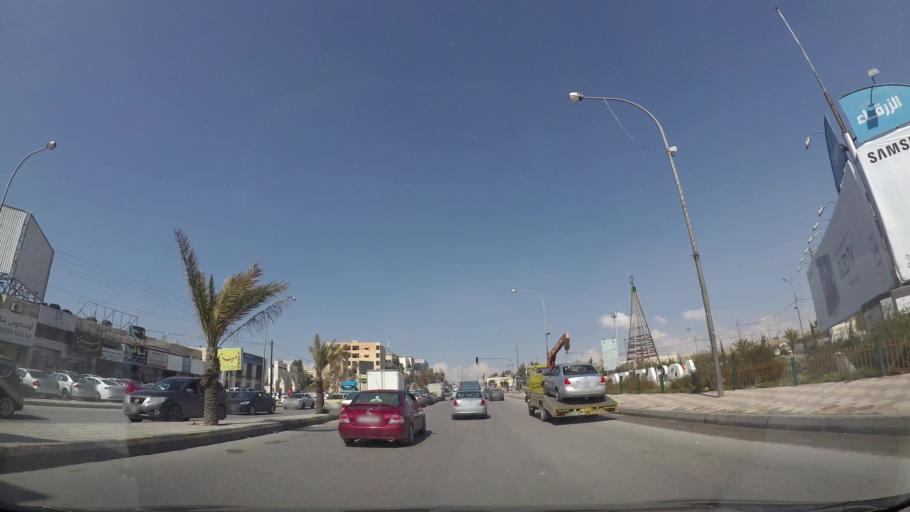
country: JO
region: Zarqa
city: Zarqa
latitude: 32.0506
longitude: 36.0929
